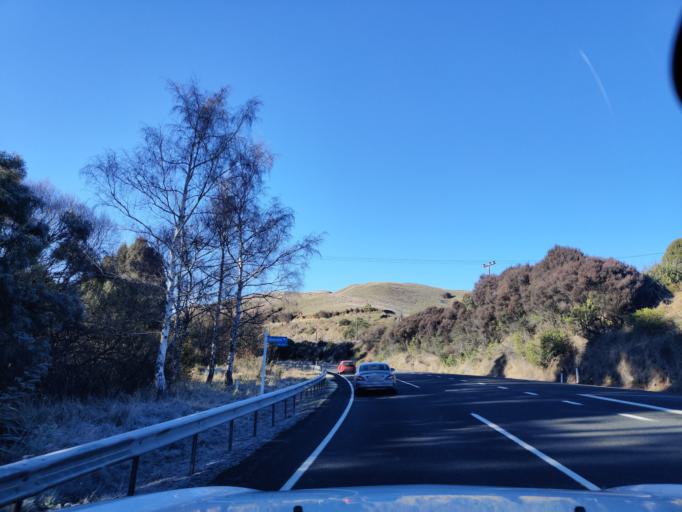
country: NZ
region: Manawatu-Wanganui
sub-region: Ruapehu District
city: Waiouru
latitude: -39.5668
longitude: 175.6984
